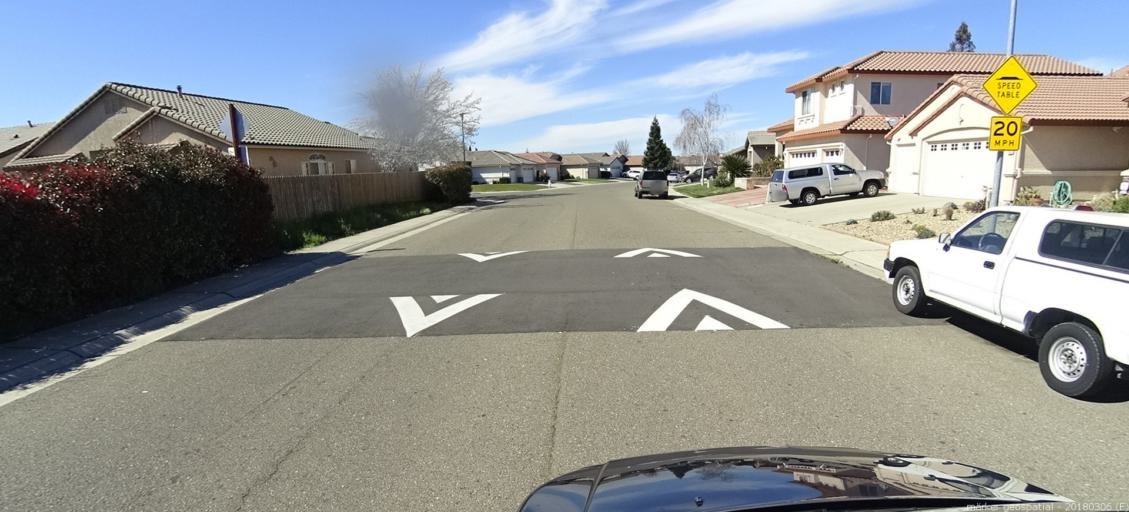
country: US
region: California
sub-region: Sacramento County
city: Vineyard
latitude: 38.4692
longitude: -121.3558
